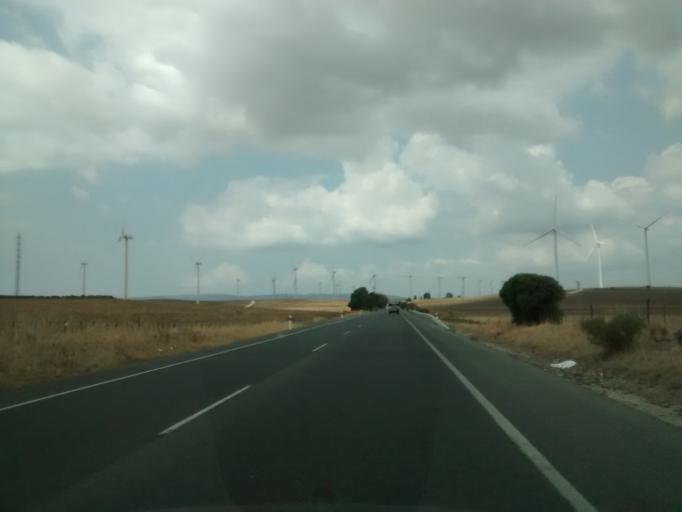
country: ES
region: Andalusia
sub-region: Provincia de Cadiz
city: Zahara de los Atunes
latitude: 36.1517
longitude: -5.7230
